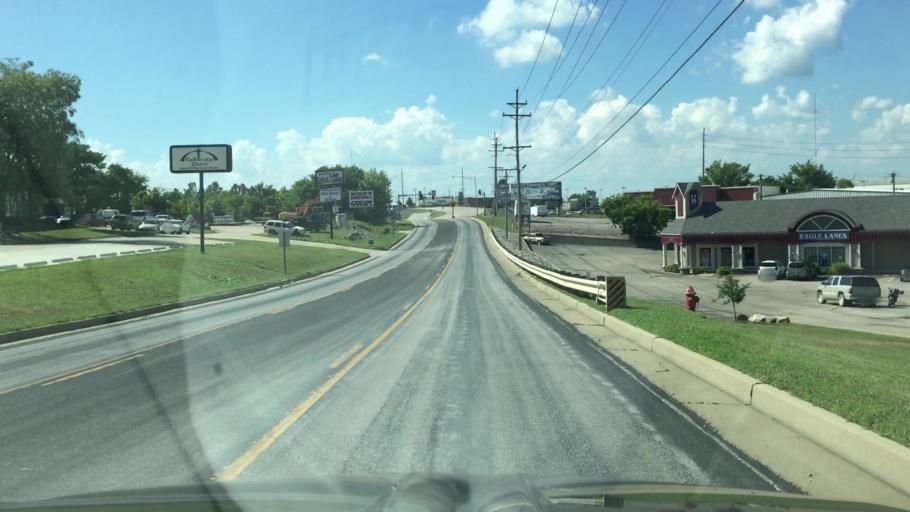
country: US
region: Missouri
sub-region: Camden County
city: Osage Beach
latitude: 38.1527
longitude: -92.6013
